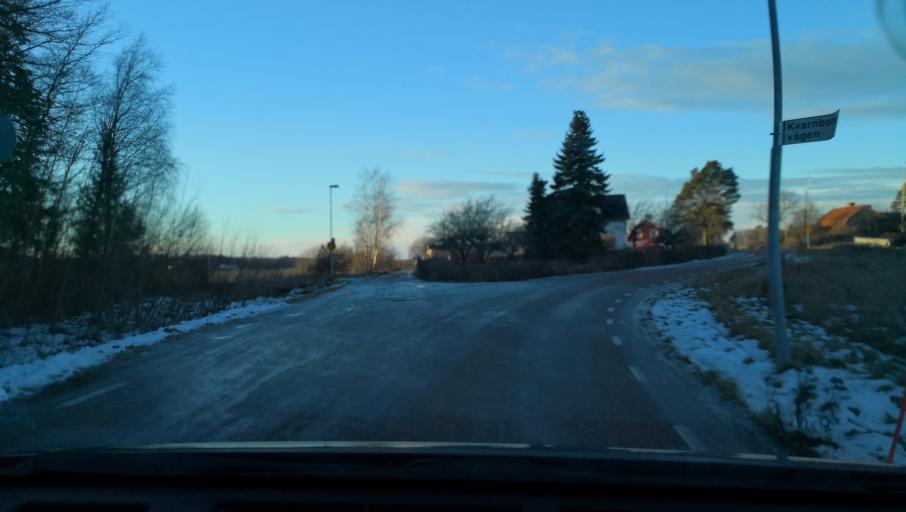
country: SE
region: Vaestmanland
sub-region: Vasteras
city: Tillberga
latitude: 59.6891
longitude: 16.6115
